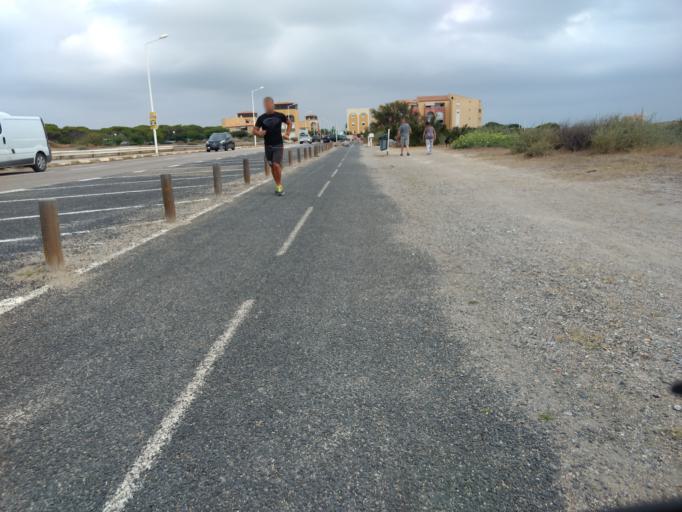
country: FR
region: Languedoc-Roussillon
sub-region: Departement des Pyrenees-Orientales
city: Le Barcares
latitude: 42.8446
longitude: 3.0423
